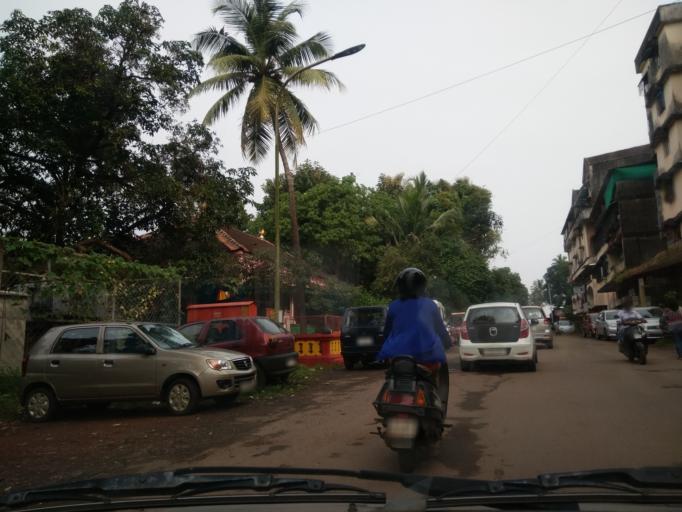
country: IN
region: Goa
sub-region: South Goa
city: Madgaon
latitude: 15.2736
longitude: 73.9551
